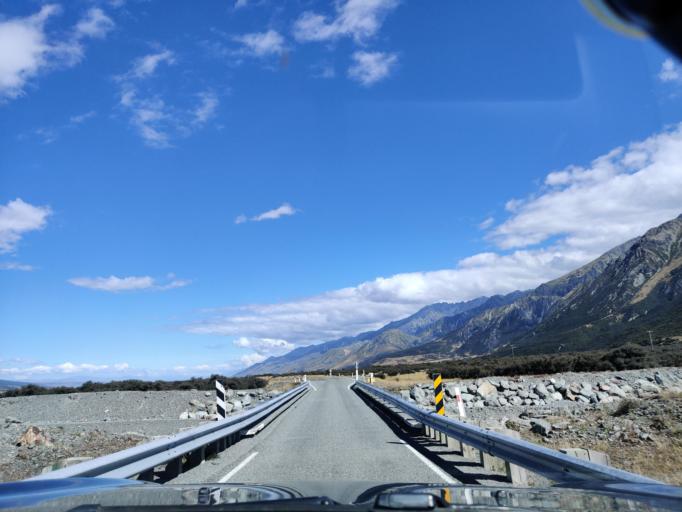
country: NZ
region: Canterbury
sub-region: Timaru District
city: Pleasant Point
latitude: -43.7690
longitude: 170.1231
